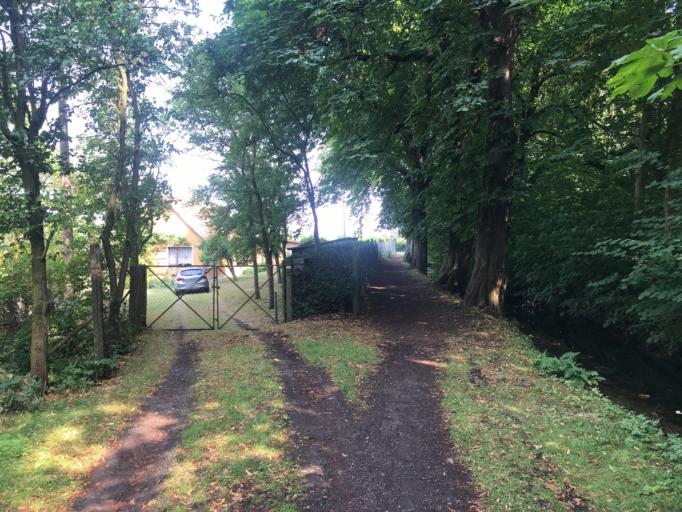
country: DE
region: Thuringia
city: Muehlhausen
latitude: 51.2237
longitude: 10.4326
